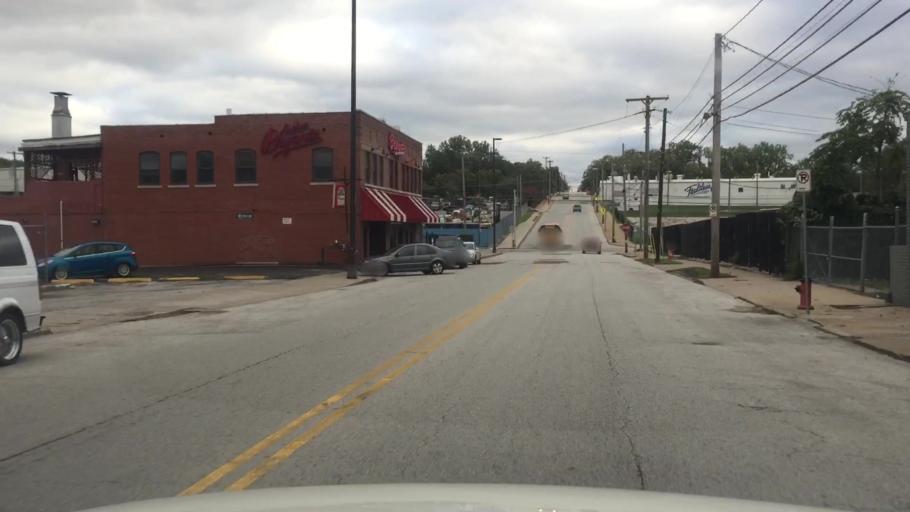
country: US
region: Missouri
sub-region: Jackson County
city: Kansas City
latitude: 39.0920
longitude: -94.5564
